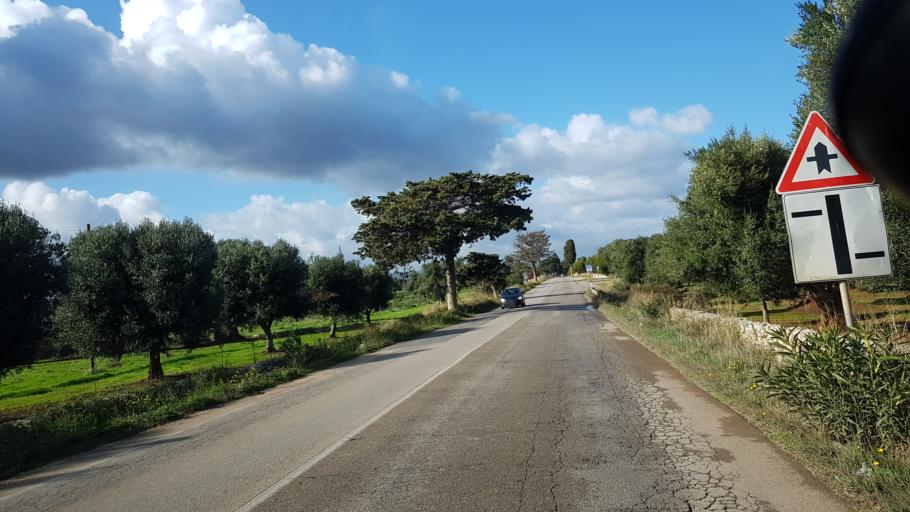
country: IT
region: Apulia
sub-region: Provincia di Brindisi
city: Pezze di Greco
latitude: 40.7987
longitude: 17.4443
